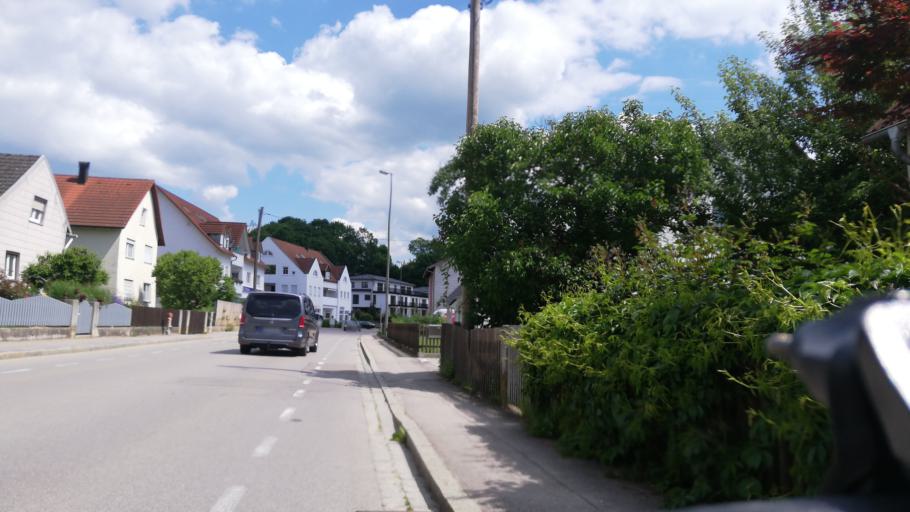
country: DE
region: Bavaria
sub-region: Upper Bavaria
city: Pfaffenhofen an der Ilm
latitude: 48.5336
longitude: 11.4945
